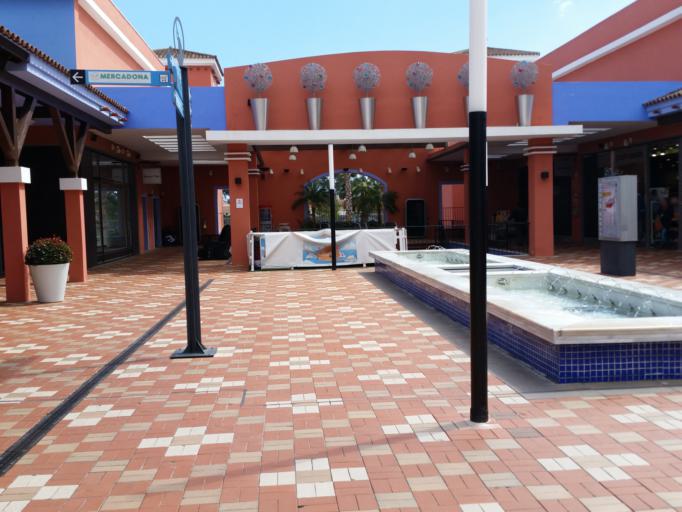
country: ES
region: Andalusia
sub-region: Provincia de Malaga
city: Torremolinos
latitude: 36.6572
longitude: -4.4769
